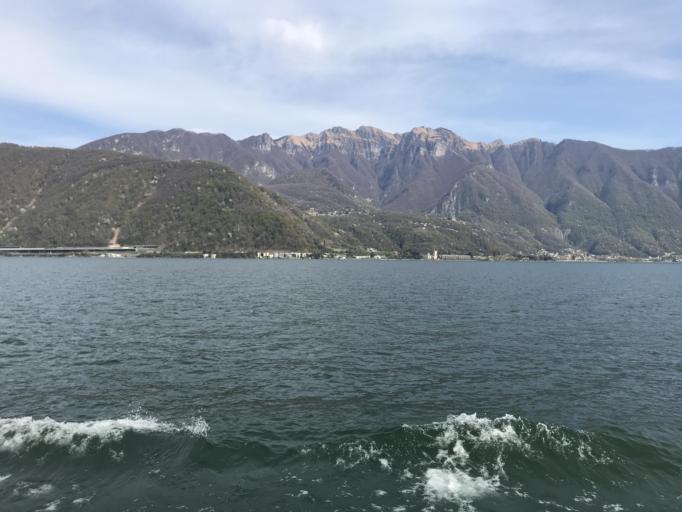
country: CH
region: Ticino
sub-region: Lugano District
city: Melide
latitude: 45.9411
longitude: 8.9446
